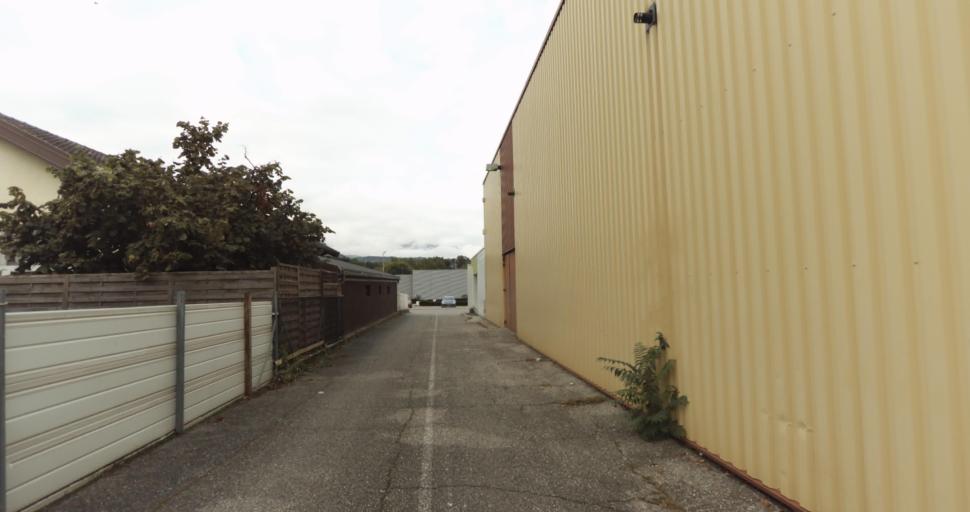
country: FR
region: Rhone-Alpes
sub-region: Departement de la Savoie
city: La Ravoire
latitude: 45.5670
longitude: 5.9676
